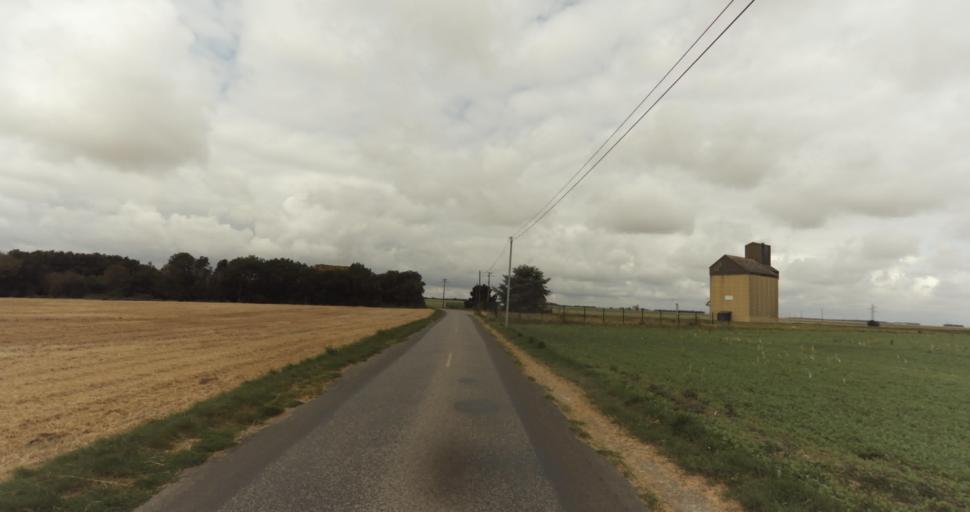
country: FR
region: Haute-Normandie
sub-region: Departement de l'Eure
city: La Couture-Boussey
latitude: 48.9314
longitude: 1.3459
